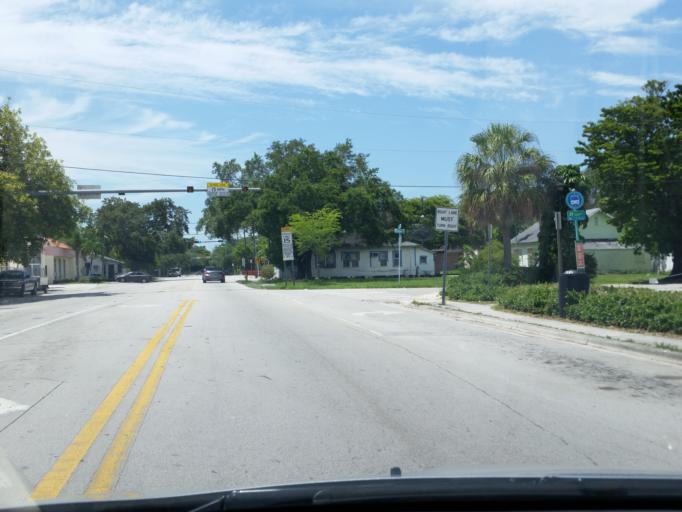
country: US
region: Florida
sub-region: Miami-Dade County
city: Coconut Grove
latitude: 25.7276
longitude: -80.2536
